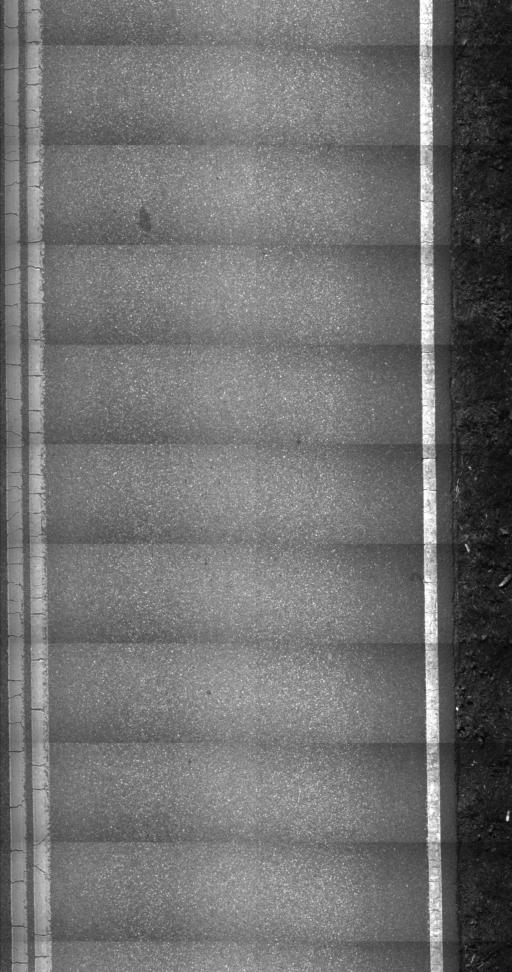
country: US
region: Vermont
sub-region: Lamoille County
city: Johnson
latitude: 44.5356
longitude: -72.7904
